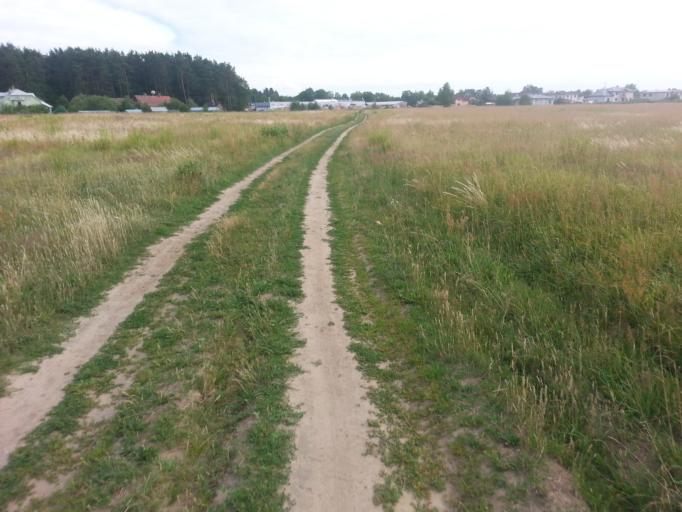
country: LV
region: Stopini
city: Ulbroka
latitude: 56.9482
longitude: 24.2612
